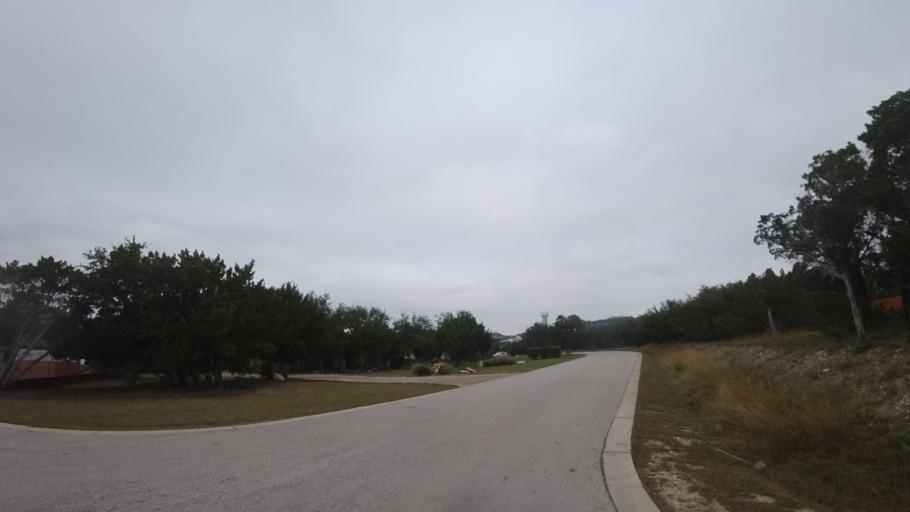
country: US
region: Texas
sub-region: Travis County
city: Hudson Bend
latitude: 30.3866
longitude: -97.9191
